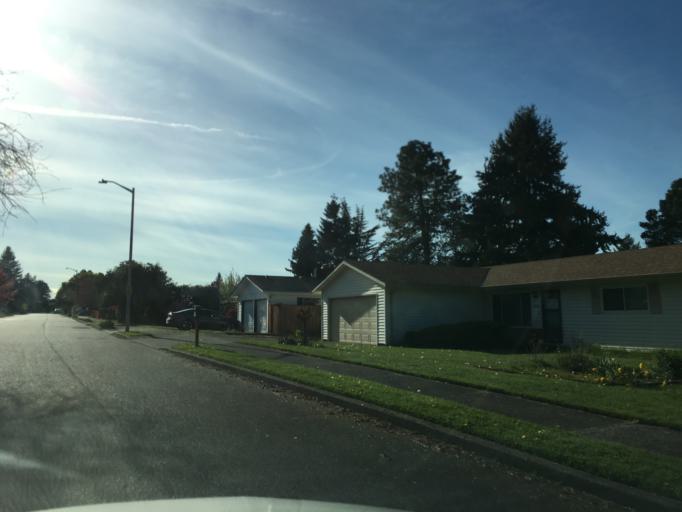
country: US
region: Oregon
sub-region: Multnomah County
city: Fairview
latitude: 45.5496
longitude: -122.5179
